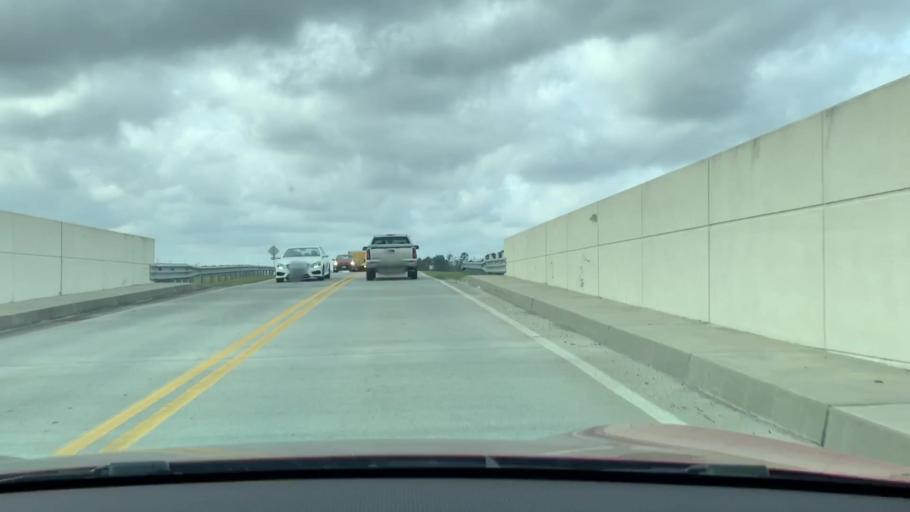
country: US
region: Georgia
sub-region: Chatham County
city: Port Wentworth
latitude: 32.1422
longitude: -81.2054
